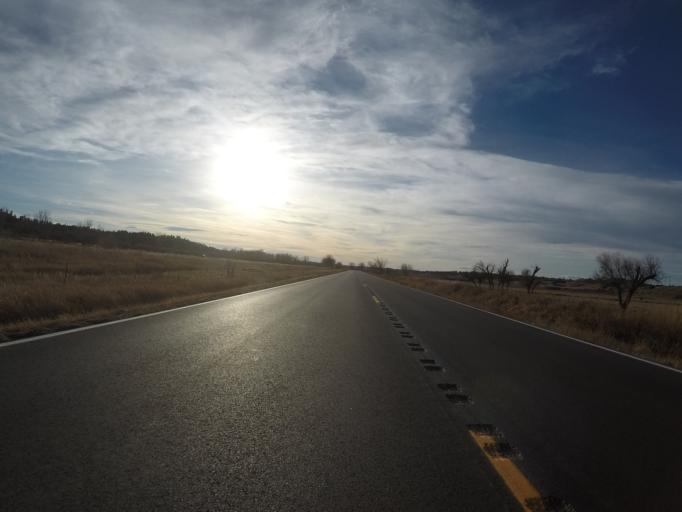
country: US
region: Montana
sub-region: Musselshell County
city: Roundup
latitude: 46.3631
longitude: -108.6579
